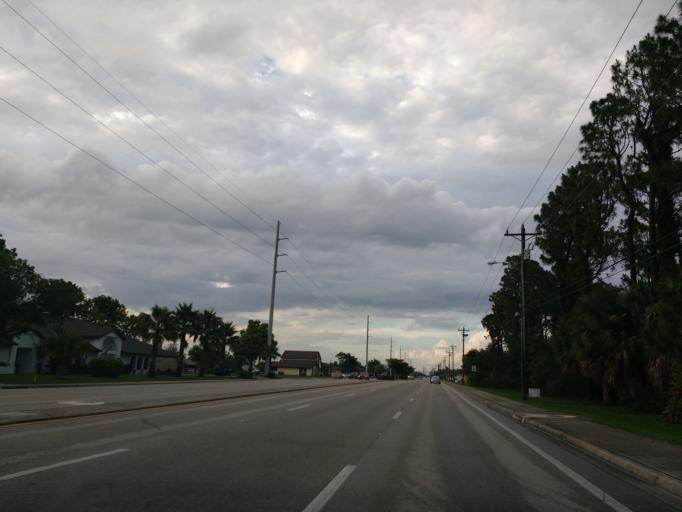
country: US
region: Florida
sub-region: Lee County
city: Lochmoor Waterway Estates
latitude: 26.6273
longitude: -81.9741
